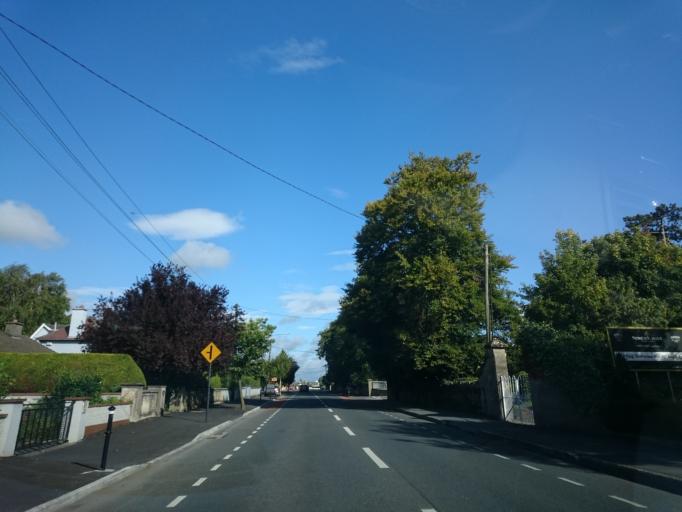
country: IE
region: Leinster
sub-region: Kilkenny
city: Kilkenny
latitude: 52.6648
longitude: -7.2516
